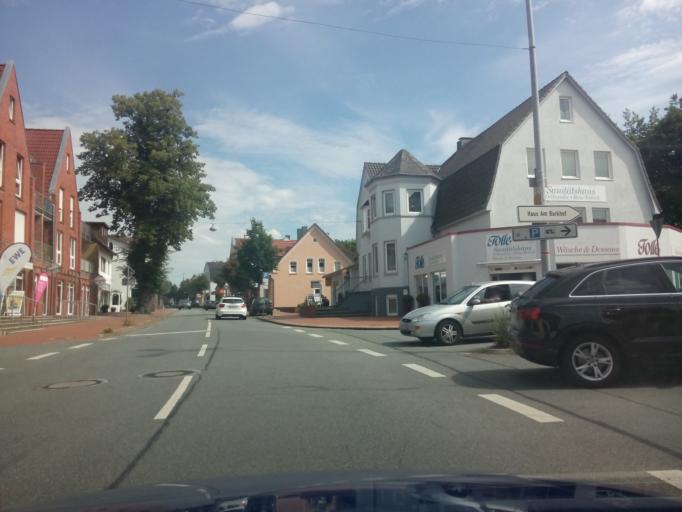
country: DE
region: Lower Saxony
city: Osterholz-Scharmbeck
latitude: 53.2271
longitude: 8.7899
